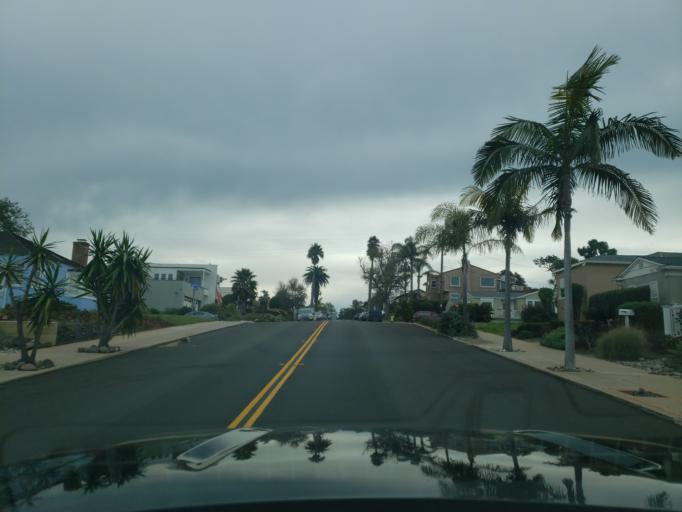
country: US
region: California
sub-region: San Diego County
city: Coronado
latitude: 32.7376
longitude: -117.2465
